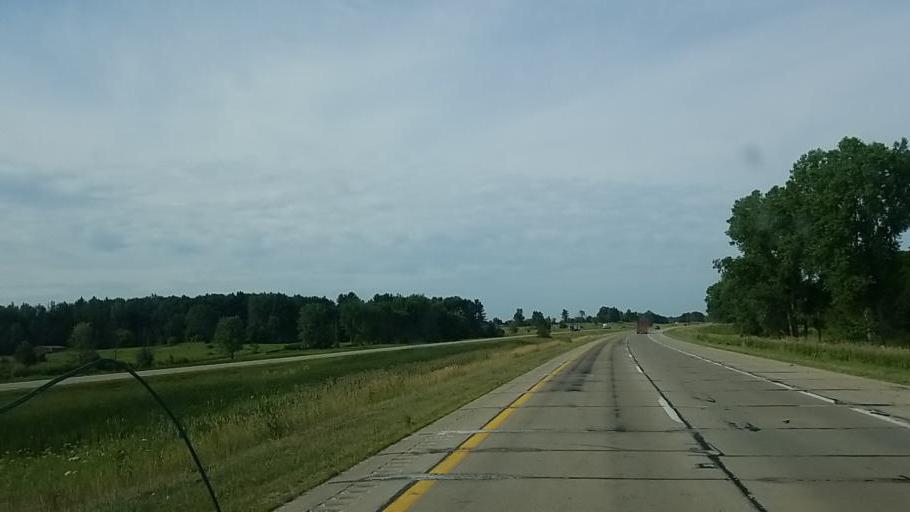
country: US
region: Michigan
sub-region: Eaton County
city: Charlotte
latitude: 42.4939
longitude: -84.8653
